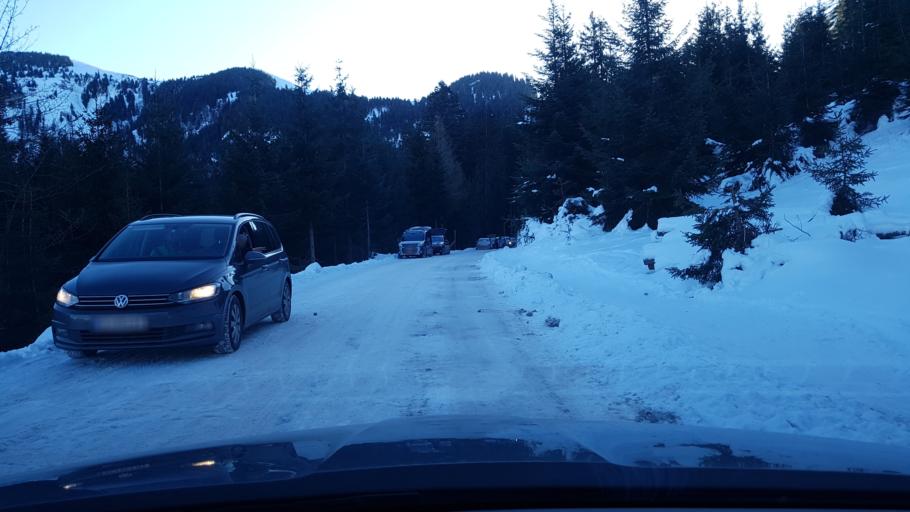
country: AT
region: Salzburg
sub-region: Politischer Bezirk Hallein
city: Scheffau am Tennengebirge
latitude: 47.6428
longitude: 13.2438
